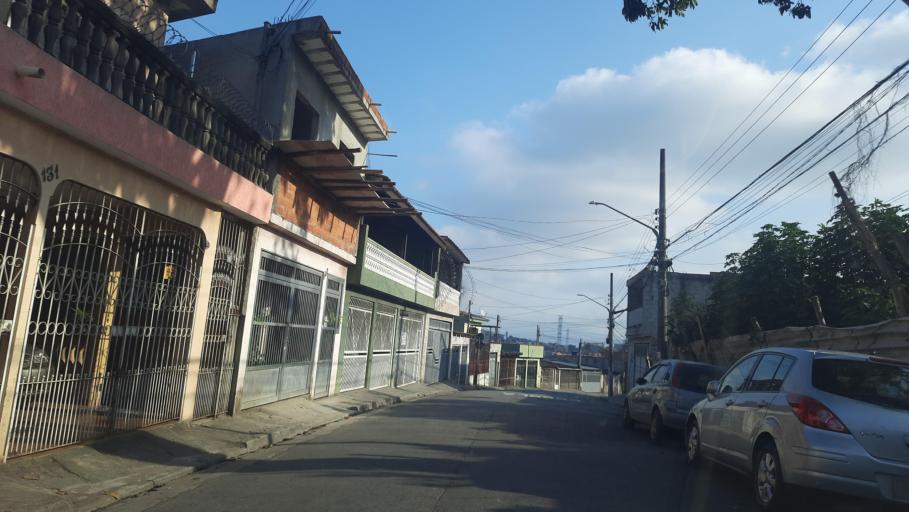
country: BR
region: Sao Paulo
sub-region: Caieiras
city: Caieiras
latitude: -23.4517
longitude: -46.7161
